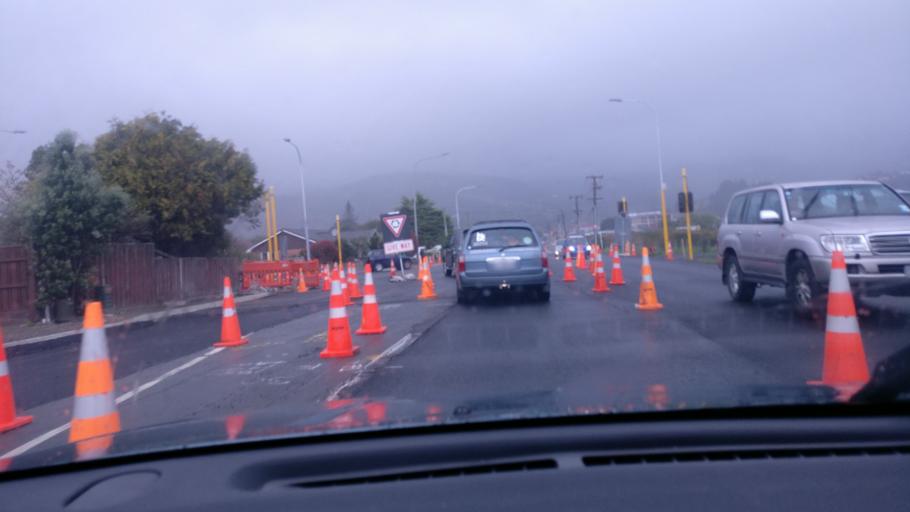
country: NZ
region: Wellington
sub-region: Kapiti Coast District
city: Paraparaumu
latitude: -40.9099
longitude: 175.0011
